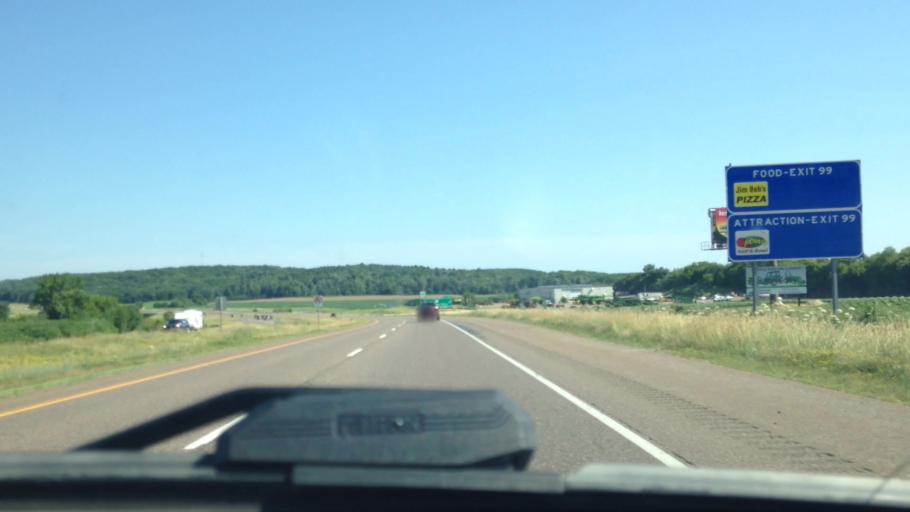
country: US
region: Wisconsin
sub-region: Chippewa County
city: Chippewa Falls
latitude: 44.9578
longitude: -91.4253
